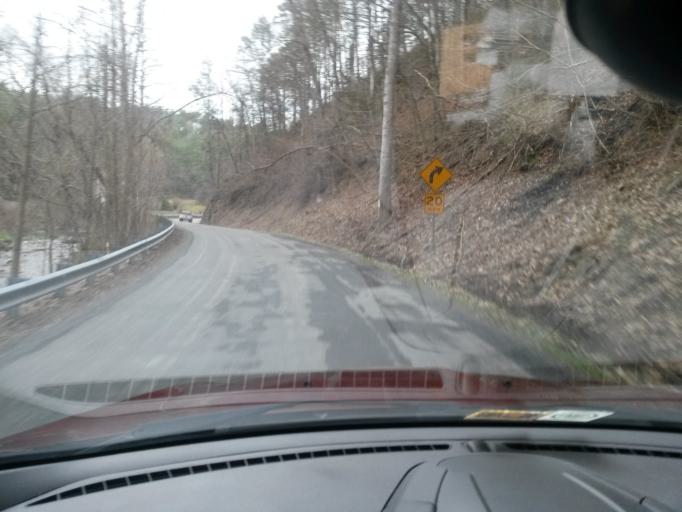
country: US
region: Virginia
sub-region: Bath County
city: Warm Springs
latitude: 38.0393
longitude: -79.8578
